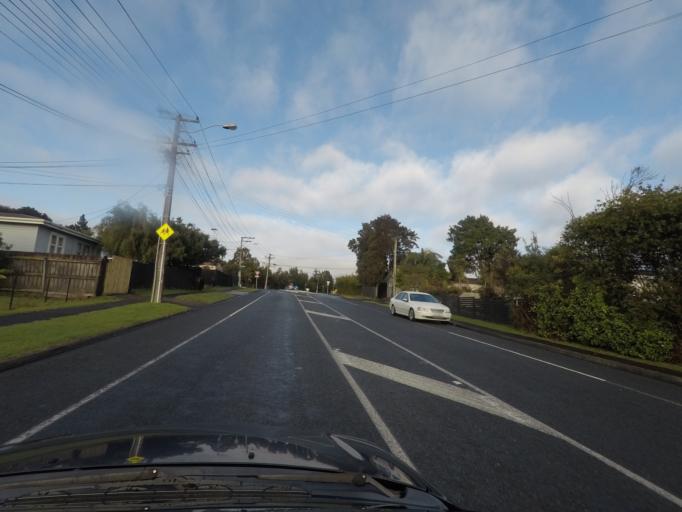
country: NZ
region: Auckland
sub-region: Auckland
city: Waitakere
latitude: -36.8998
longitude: 174.6160
